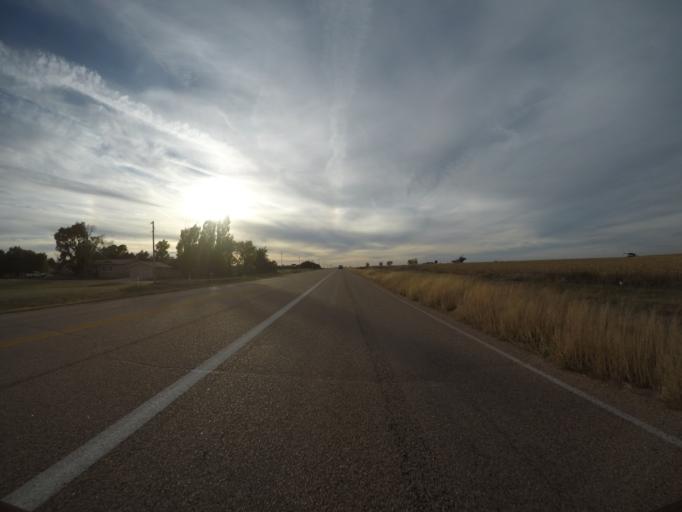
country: US
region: Colorado
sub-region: Yuma County
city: Yuma
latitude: 39.6561
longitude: -102.6223
